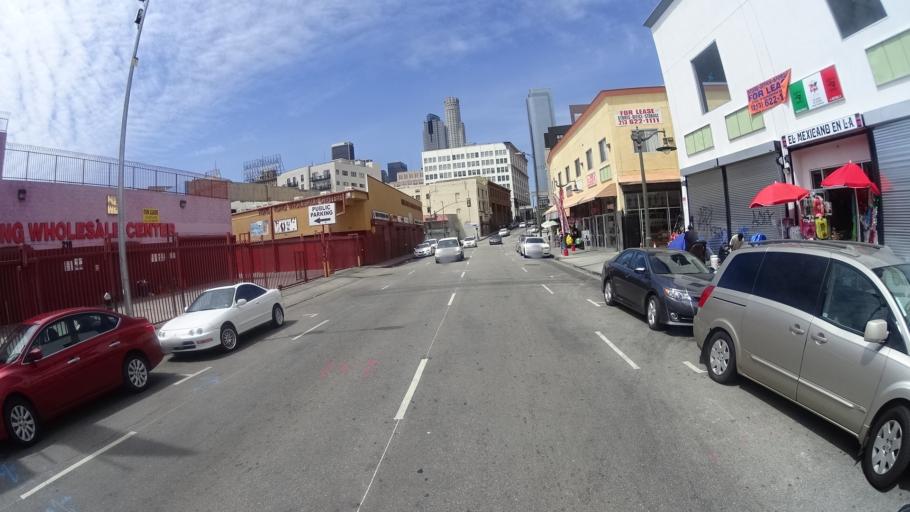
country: US
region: California
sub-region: Los Angeles County
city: Los Angeles
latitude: 34.0469
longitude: -118.2456
